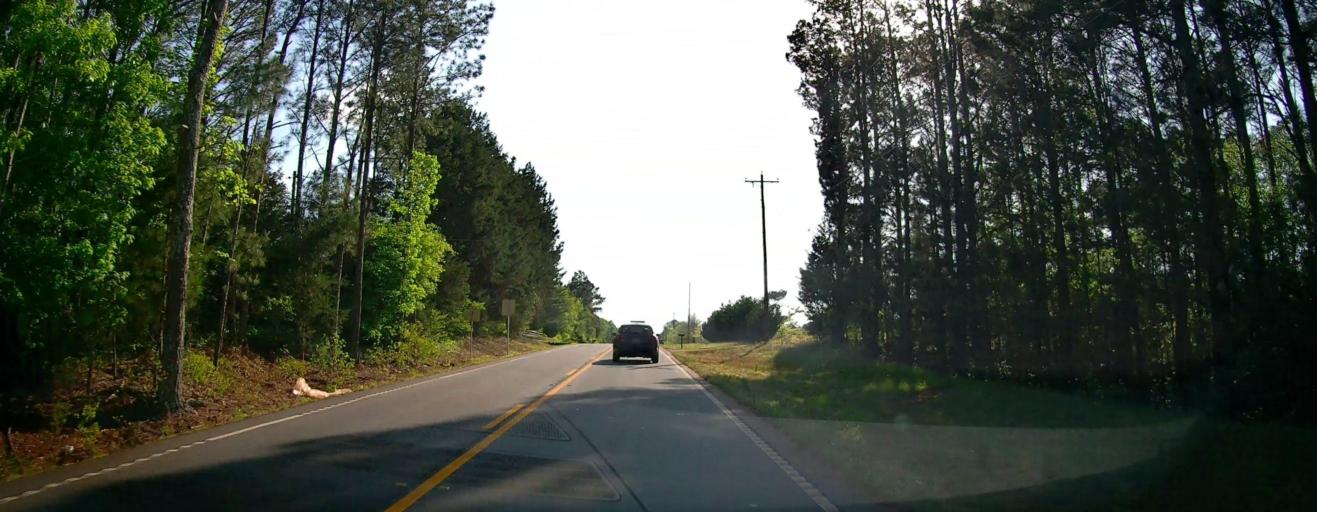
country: US
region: Georgia
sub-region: Walton County
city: Social Circle
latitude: 33.6238
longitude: -83.6814
